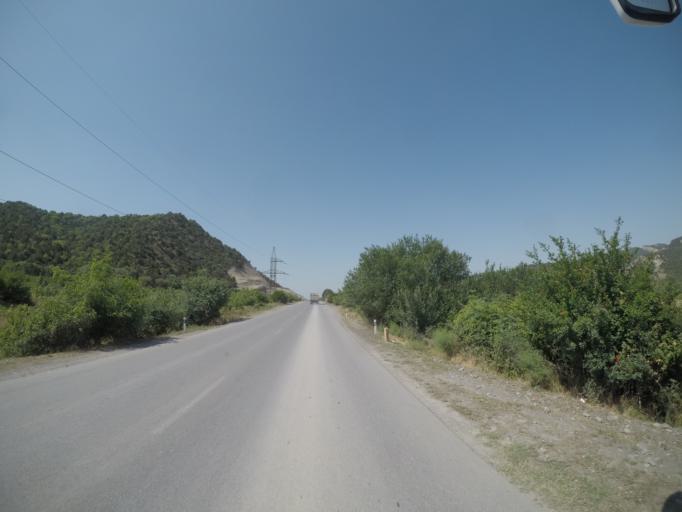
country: AZ
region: Agdas
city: Agdas
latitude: 40.7347
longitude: 47.5757
